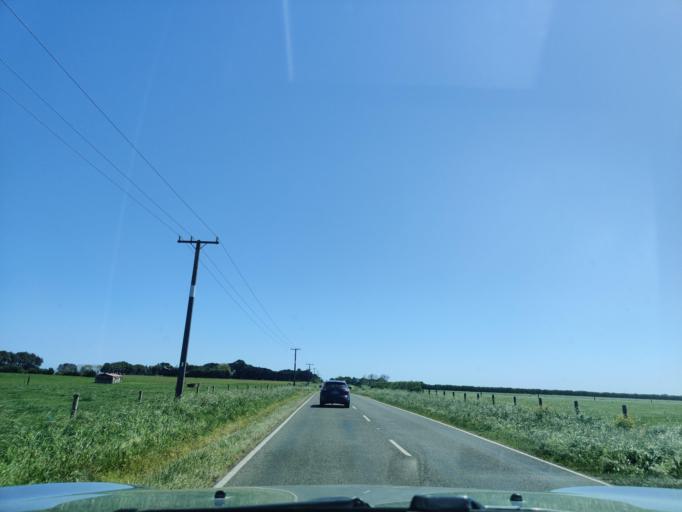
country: NZ
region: Taranaki
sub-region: South Taranaki District
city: Hawera
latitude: -39.5497
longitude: 174.1131
